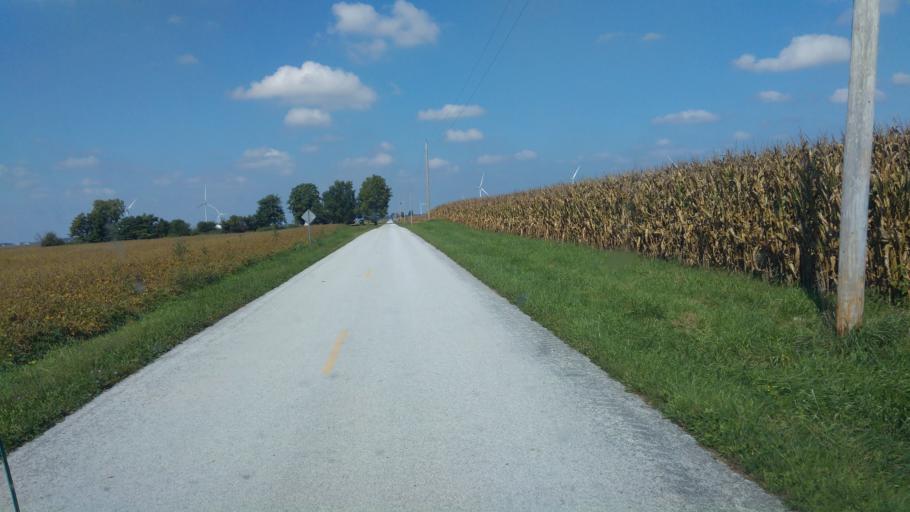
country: US
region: Ohio
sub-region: Hardin County
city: Ada
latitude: 40.7489
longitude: -83.7288
